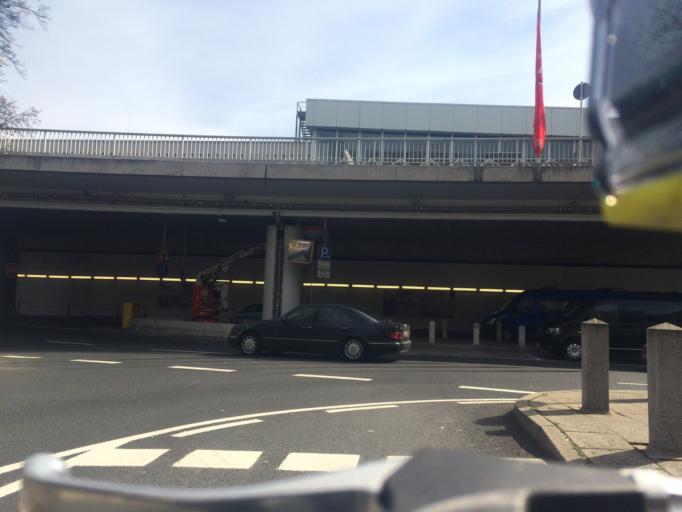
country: DE
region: Hesse
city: Kelsterbach
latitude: 50.0519
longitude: 8.5743
